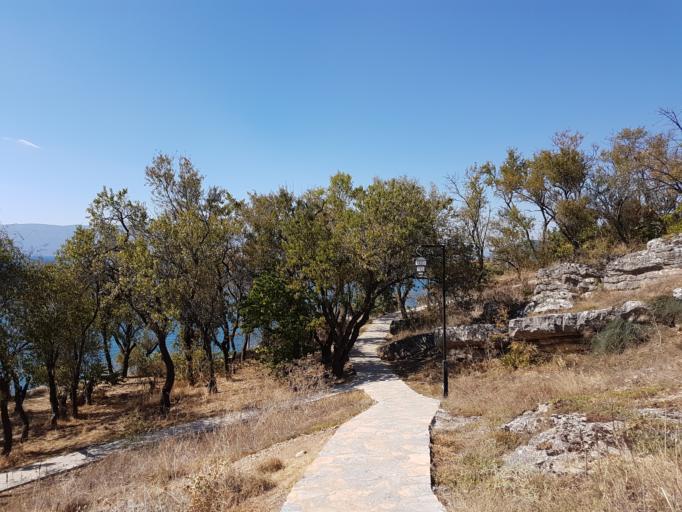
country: MK
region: Ohrid
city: Ohrid
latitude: 41.1145
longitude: 20.7880
